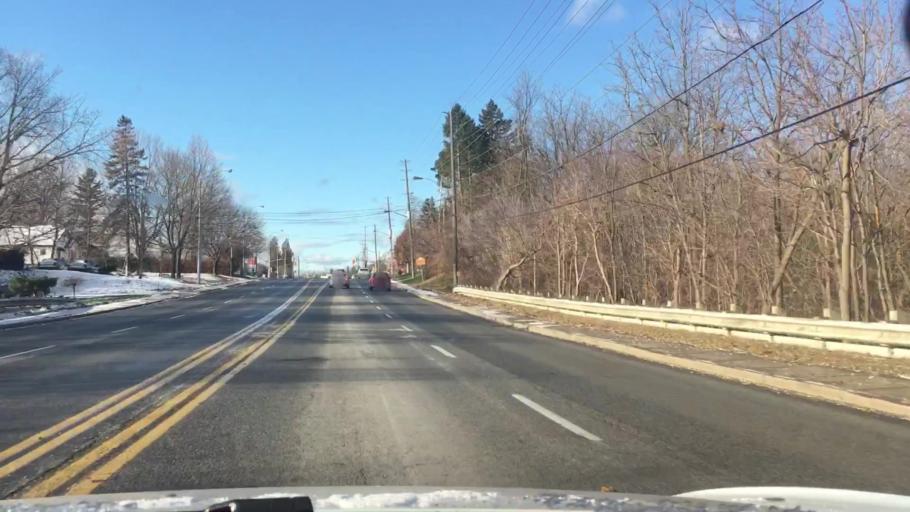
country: CA
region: Ontario
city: Markham
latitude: 43.8753
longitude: -79.2543
